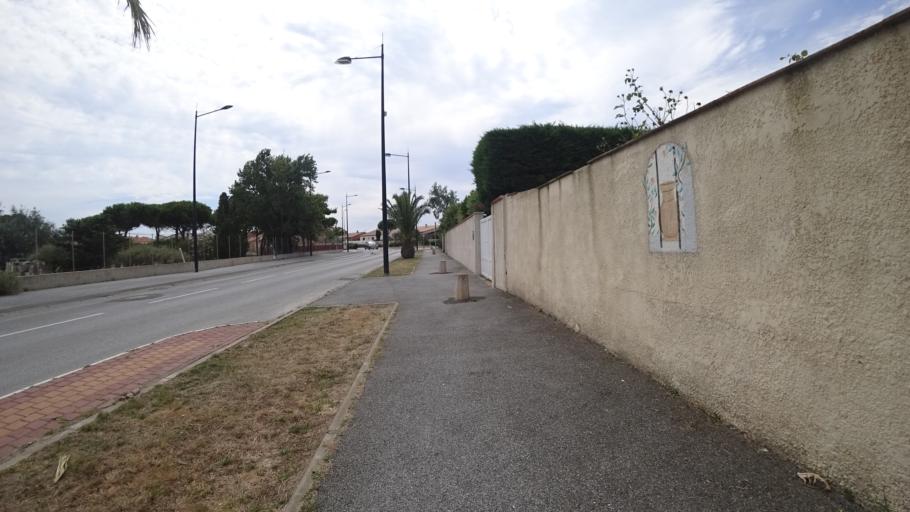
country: FR
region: Languedoc-Roussillon
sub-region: Departement des Pyrenees-Orientales
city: Le Barcares
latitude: 42.7954
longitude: 3.0319
